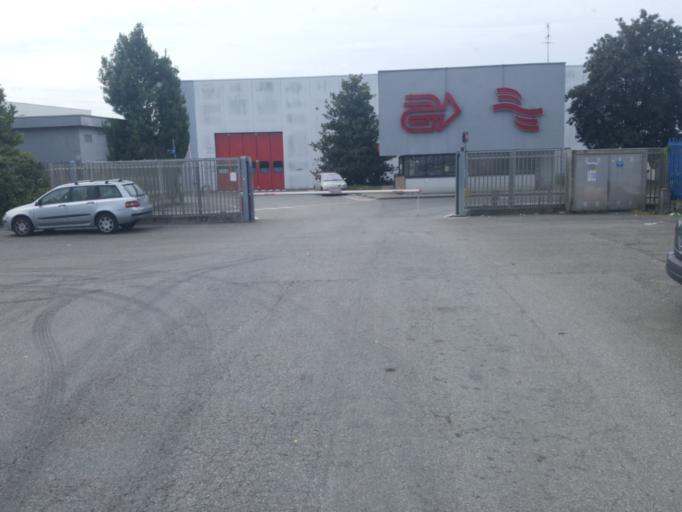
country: IT
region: Lombardy
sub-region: Provincia di Monza e Brianza
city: Cavenago di Brianza
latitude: 45.5786
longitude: 9.4021
